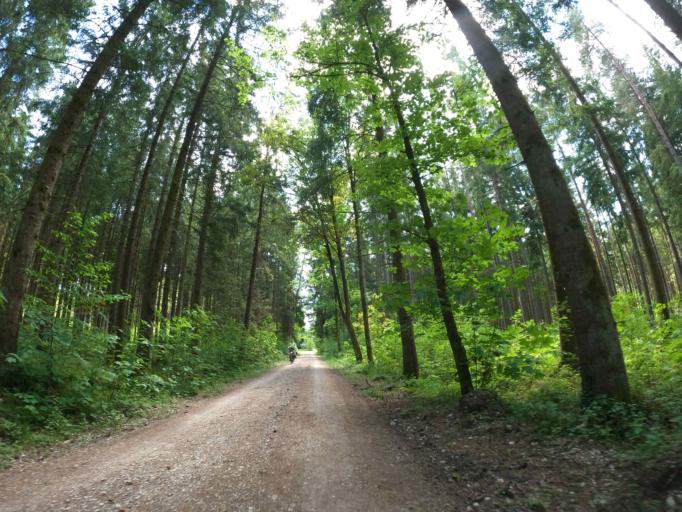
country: DE
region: Bavaria
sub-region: Upper Bavaria
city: Oberhaching
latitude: 48.0161
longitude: 11.6262
